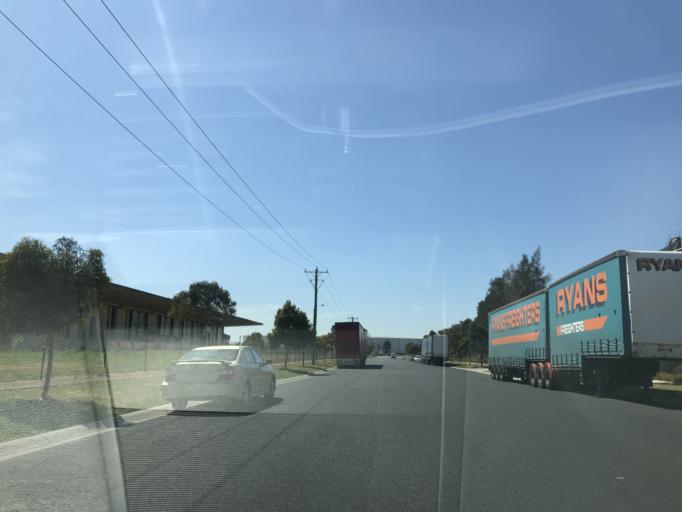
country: AU
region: Victoria
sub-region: Wyndham
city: Truganina
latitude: -37.8195
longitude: 144.7722
